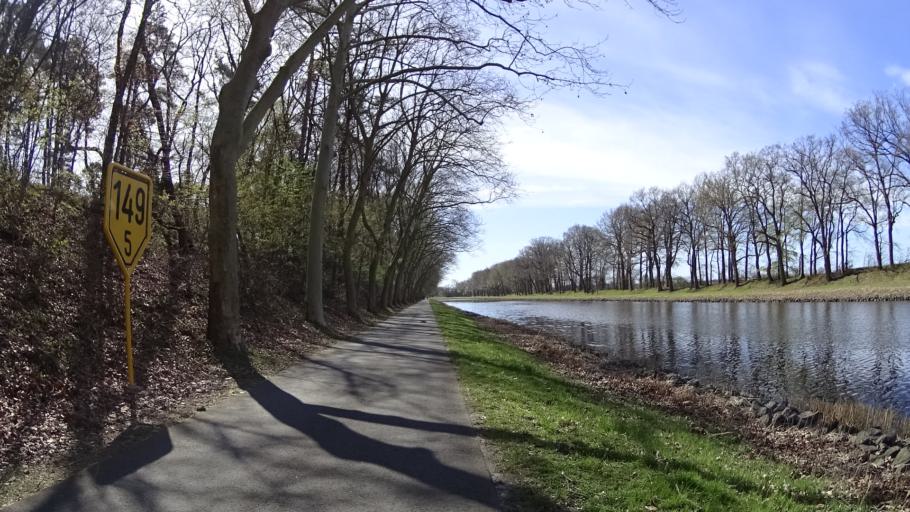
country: DE
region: Lower Saxony
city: Lingen
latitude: 52.5475
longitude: 7.2940
